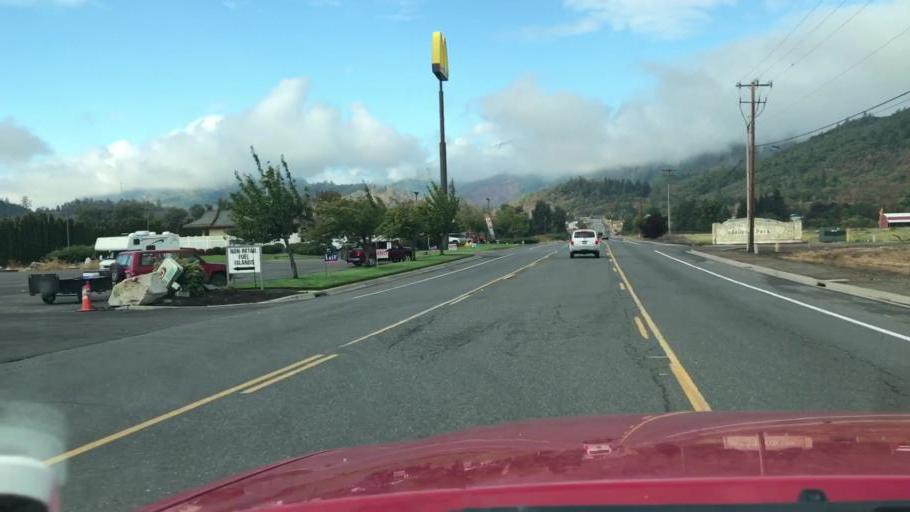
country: US
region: Oregon
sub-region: Douglas County
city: Tri-City
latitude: 42.9732
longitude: -123.3391
